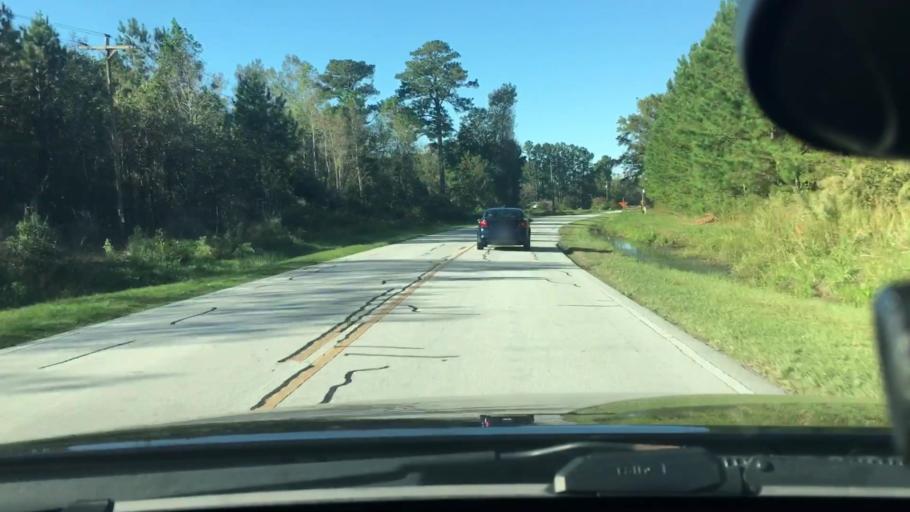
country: US
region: North Carolina
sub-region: Craven County
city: Vanceboro
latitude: 35.2835
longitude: -77.1541
